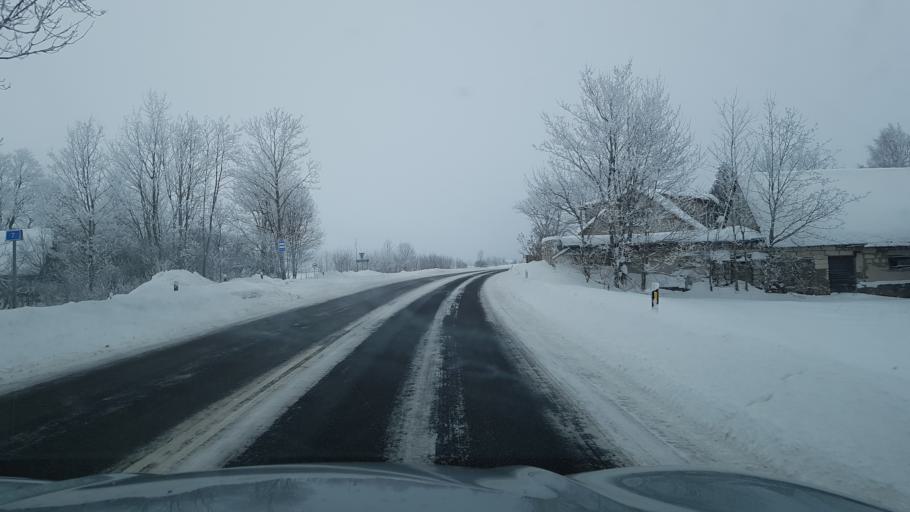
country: EE
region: Ida-Virumaa
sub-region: Johvi vald
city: Johvi
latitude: 59.3179
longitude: 27.3930
